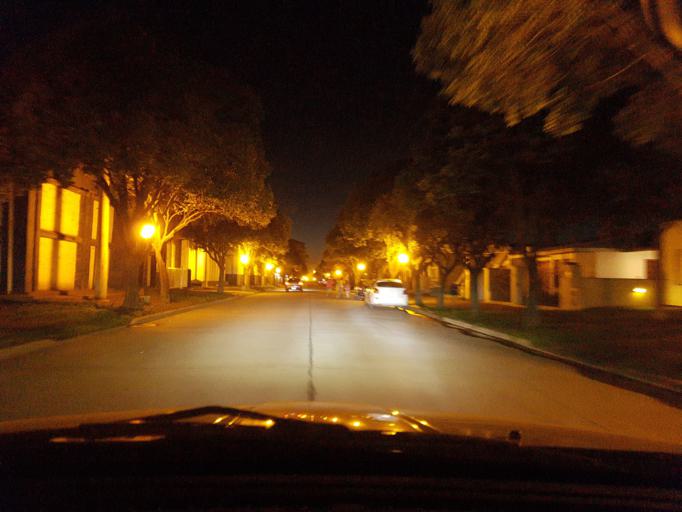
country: AR
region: Cordoba
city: General Cabrera
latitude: -32.7600
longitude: -63.7952
